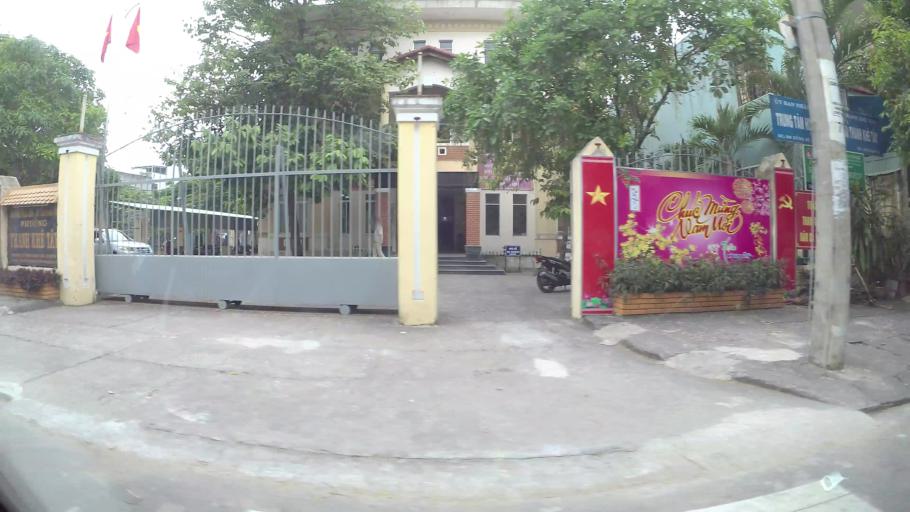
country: VN
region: Da Nang
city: Lien Chieu
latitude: 16.0770
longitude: 108.1715
